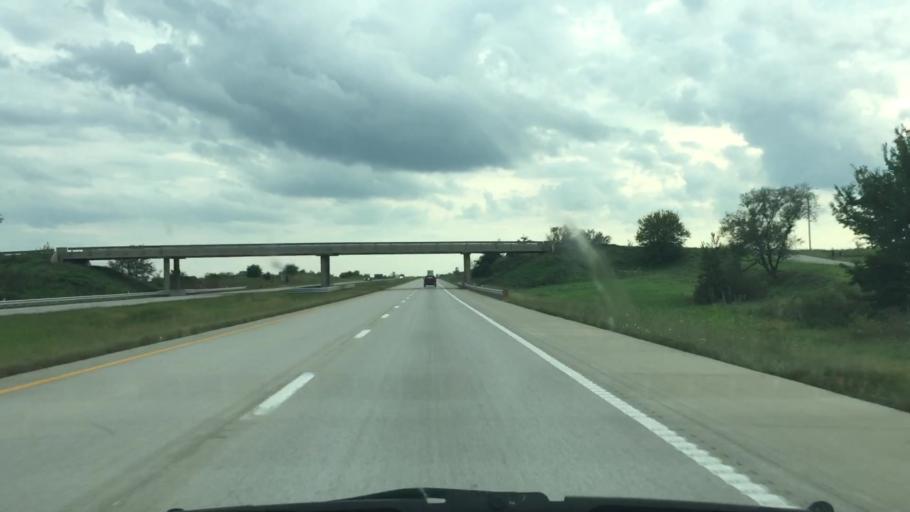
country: US
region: Missouri
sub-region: Clinton County
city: Lathrop
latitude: 39.5871
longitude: -94.2576
